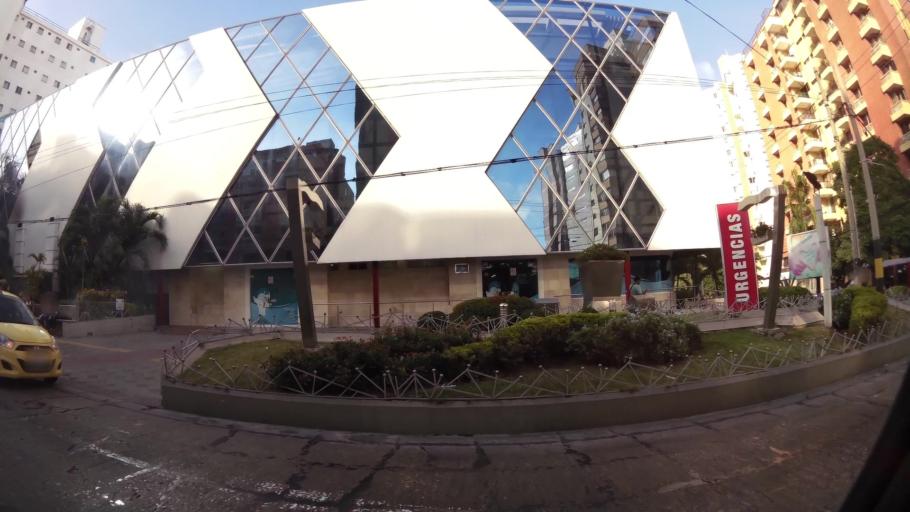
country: CO
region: Atlantico
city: Barranquilla
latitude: 11.0019
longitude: -74.8160
